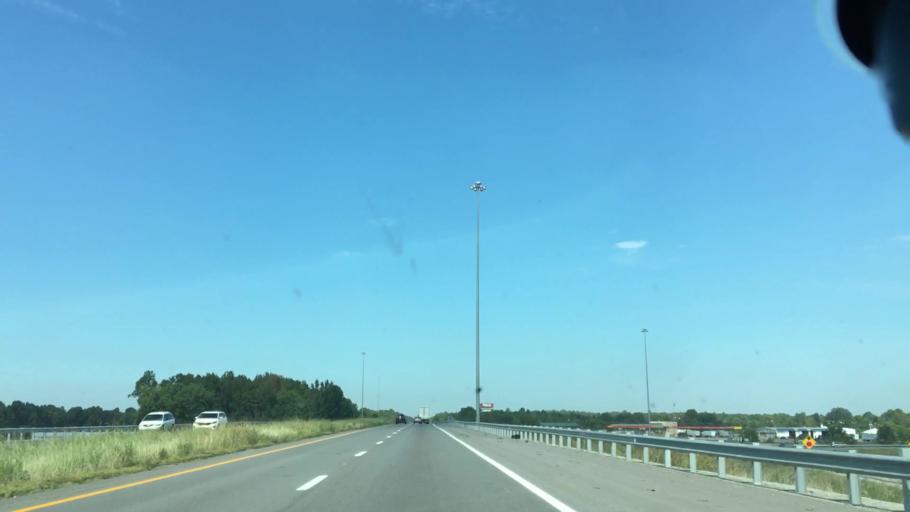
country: US
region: Kentucky
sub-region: Hopkins County
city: Nortonville
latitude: 37.2501
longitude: -87.4496
